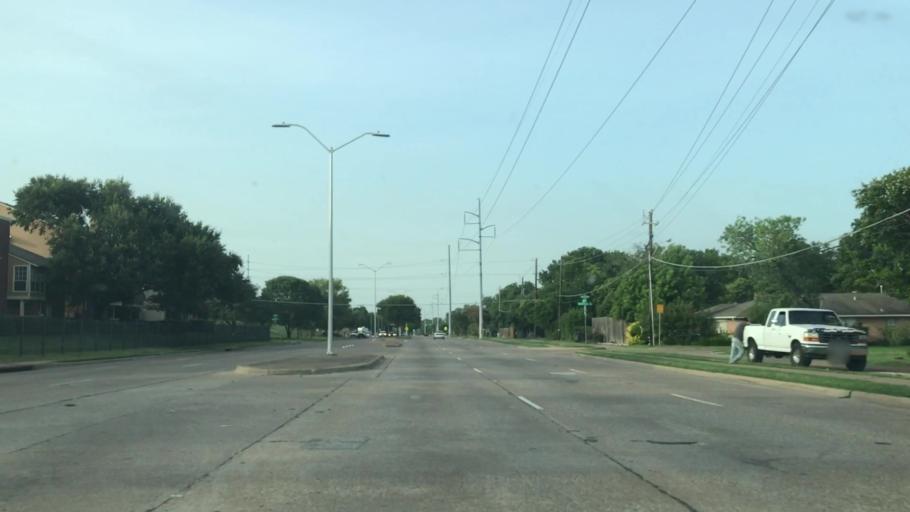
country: US
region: Texas
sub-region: Dallas County
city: Balch Springs
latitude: 32.7897
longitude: -96.7001
